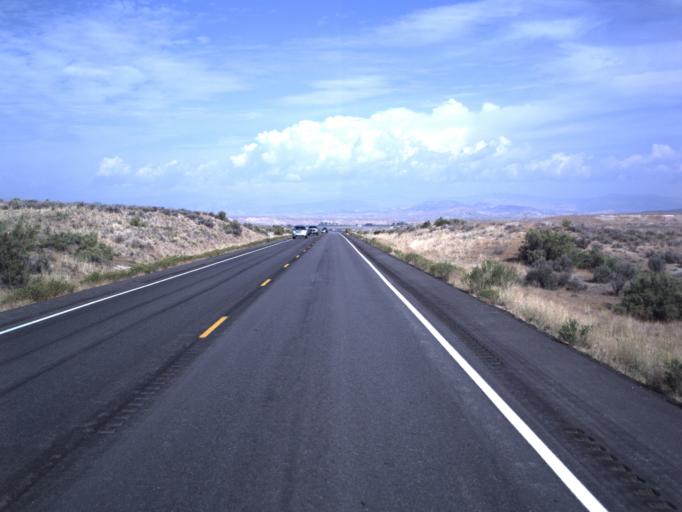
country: US
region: Utah
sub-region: Uintah County
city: Naples
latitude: 40.3525
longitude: -109.3091
